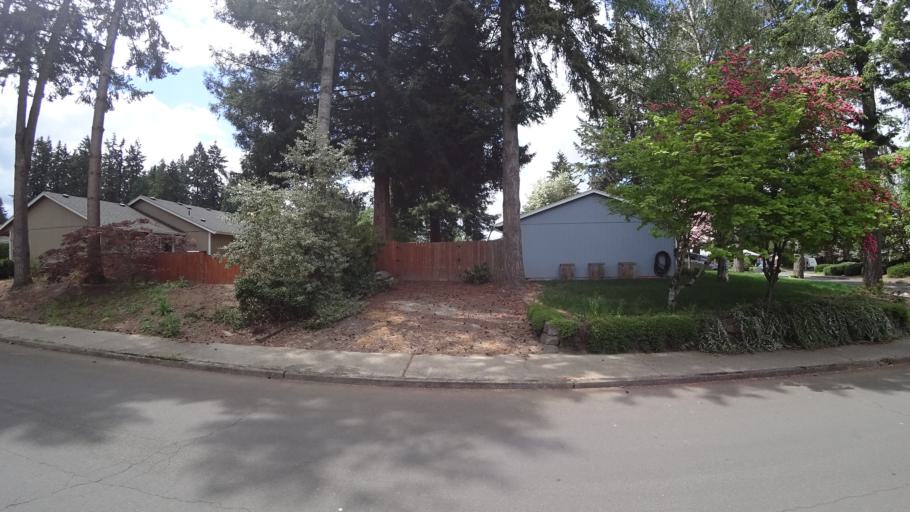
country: US
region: Oregon
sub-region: Washington County
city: Aloha
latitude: 45.4732
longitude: -122.8552
